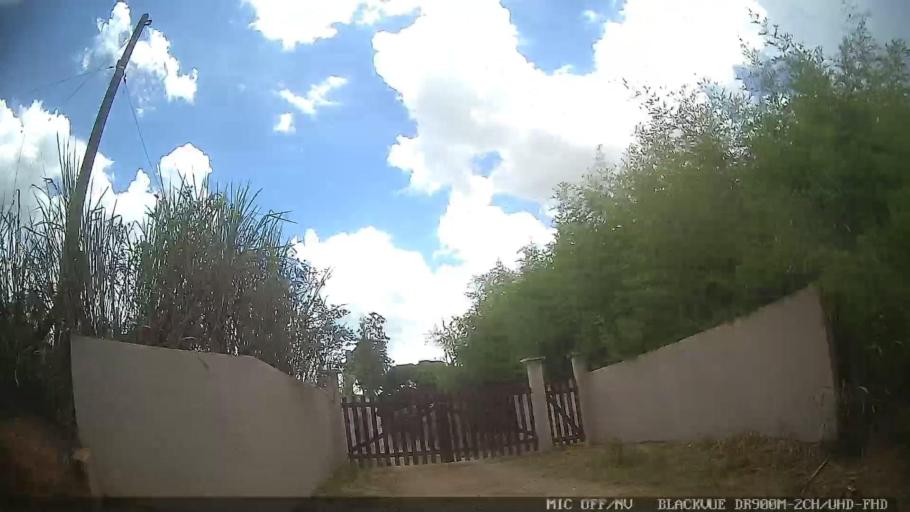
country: BR
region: Sao Paulo
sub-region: Atibaia
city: Atibaia
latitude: -23.1426
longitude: -46.6161
